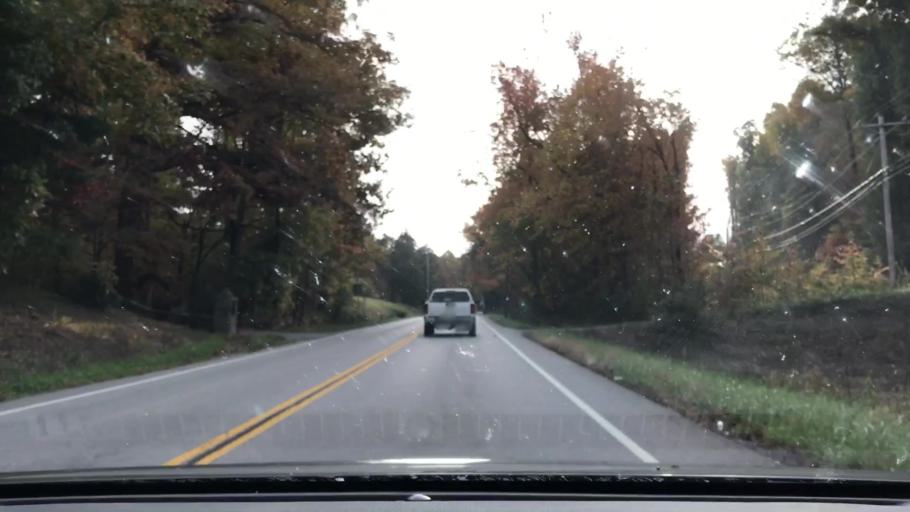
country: US
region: Tennessee
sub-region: Putnam County
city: Monterey
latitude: 36.1398
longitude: -85.2530
